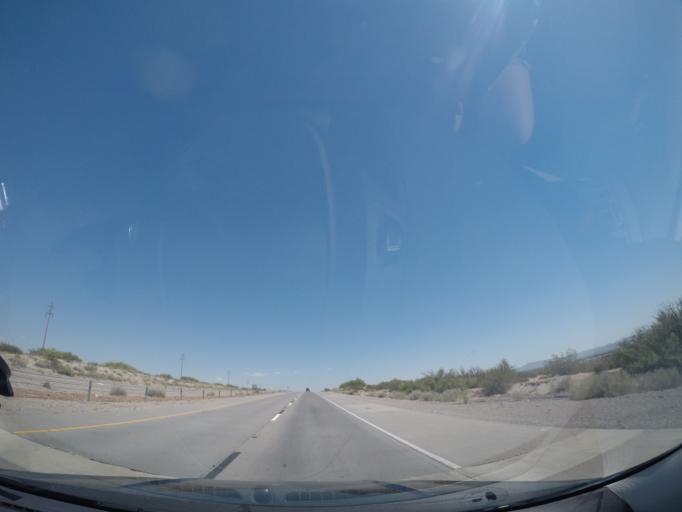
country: US
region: Texas
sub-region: El Paso County
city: Fabens
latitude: 31.5424
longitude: -106.1491
